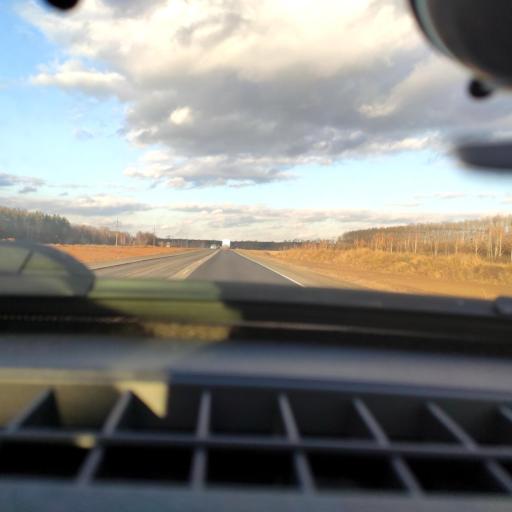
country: RU
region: Bashkortostan
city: Kabakovo
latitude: 54.7104
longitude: 56.2271
